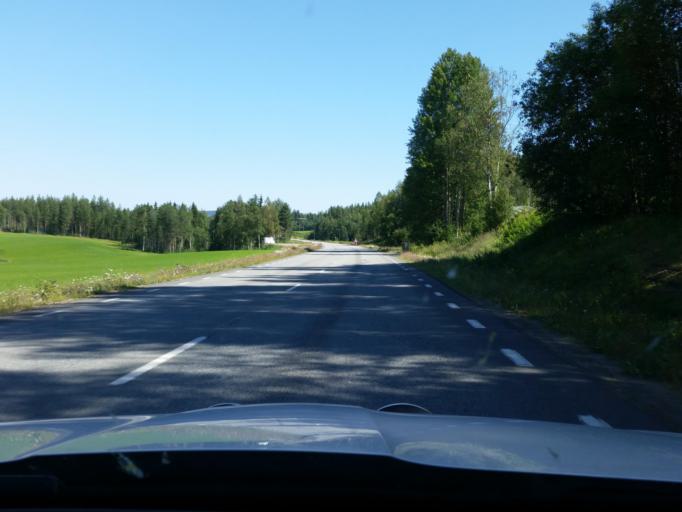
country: SE
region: Norrbotten
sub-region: Alvsbyns Kommun
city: AElvsbyn
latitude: 65.6667
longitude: 20.8965
